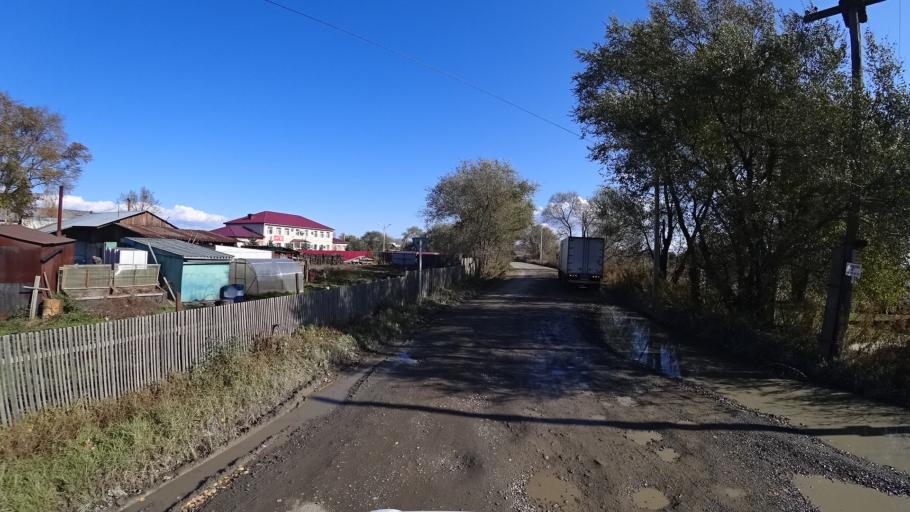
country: RU
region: Khabarovsk Krai
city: Amursk
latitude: 50.0942
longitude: 136.5007
